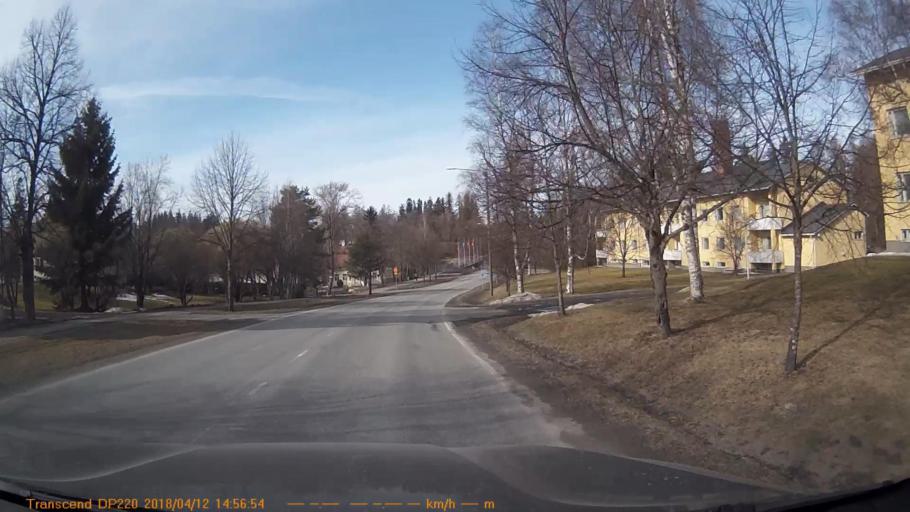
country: FI
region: Haeme
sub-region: Forssa
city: Jokioinen
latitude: 60.8105
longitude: 23.4828
